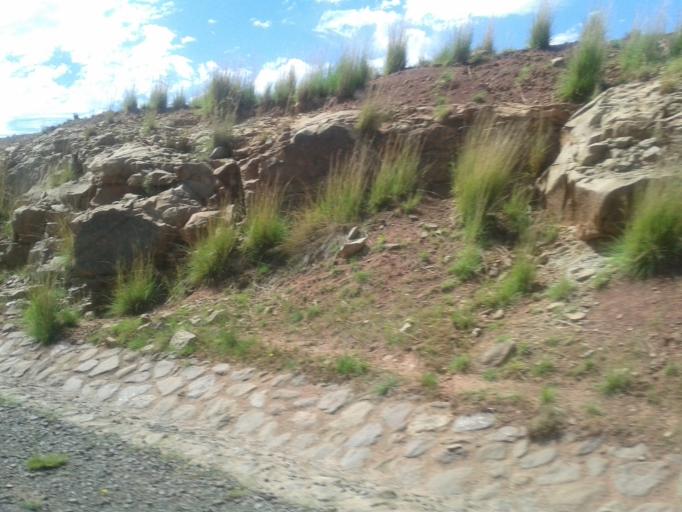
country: LS
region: Qacha's Nek
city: Qacha's Nek
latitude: -30.0387
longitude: 28.3381
